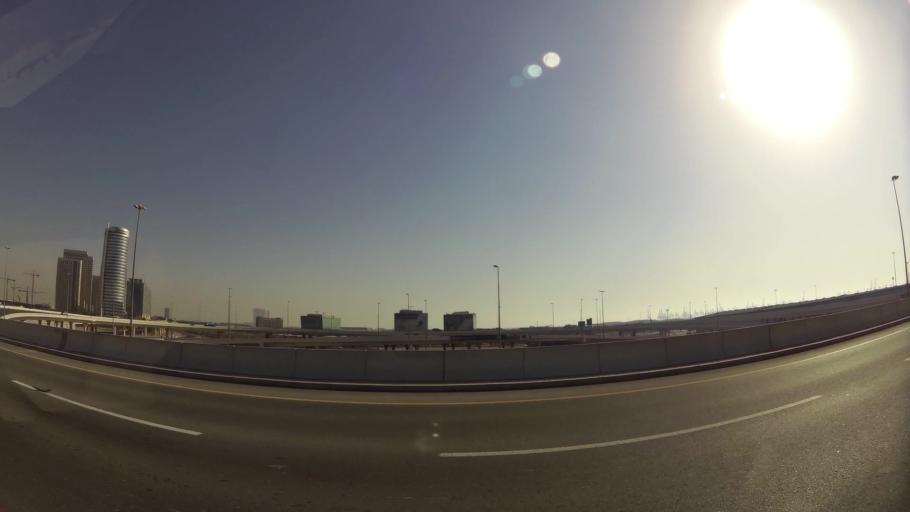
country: AE
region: Dubai
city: Dubai
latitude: 24.9895
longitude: 55.0946
